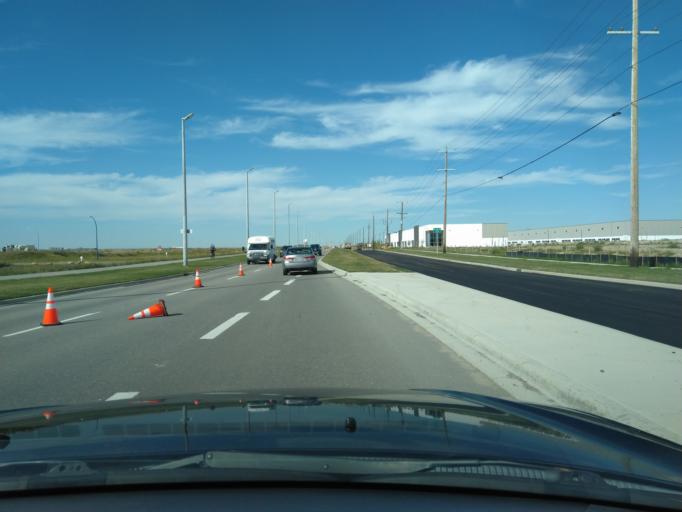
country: CA
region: Alberta
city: Calgary
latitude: 51.1267
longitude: -113.9817
